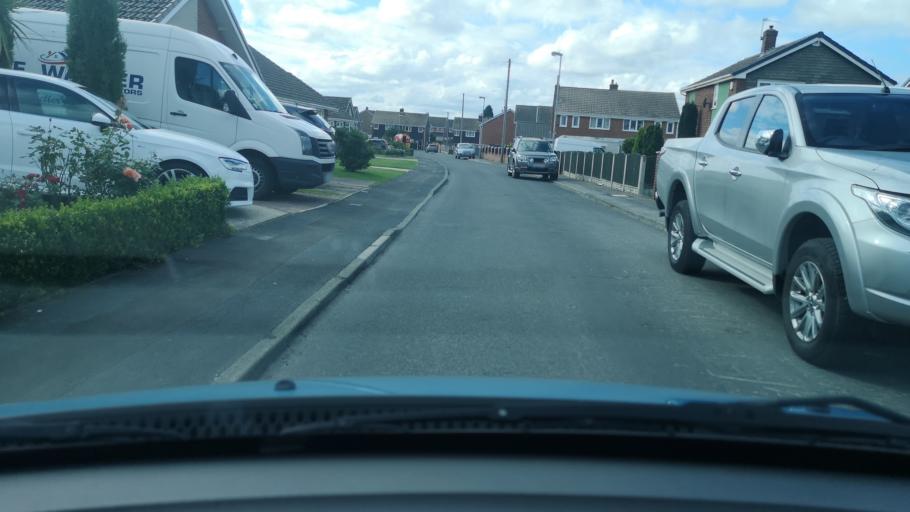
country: GB
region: England
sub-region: City and Borough of Wakefield
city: Featherstone
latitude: 53.6712
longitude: -1.3541
